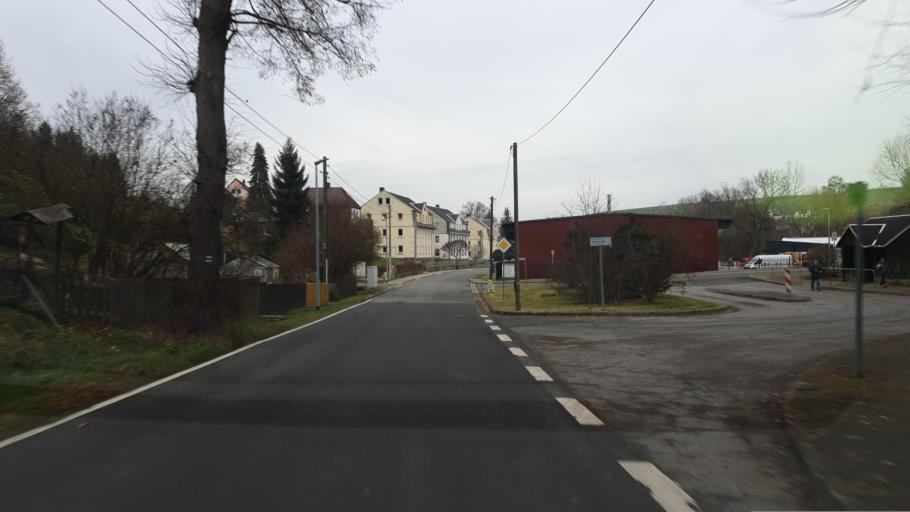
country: DE
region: Saxony
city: Mulda
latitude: 50.8055
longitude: 13.4064
